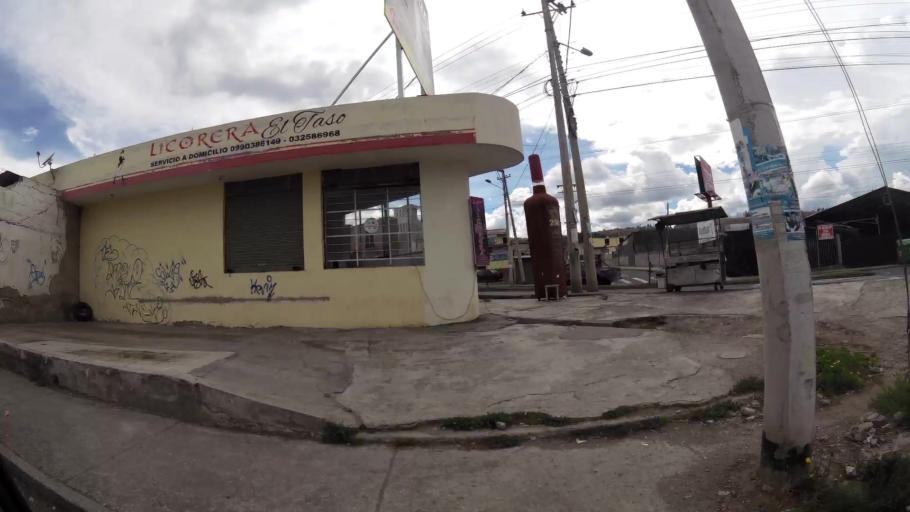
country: EC
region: Tungurahua
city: Ambato
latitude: -1.2799
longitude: -78.6306
